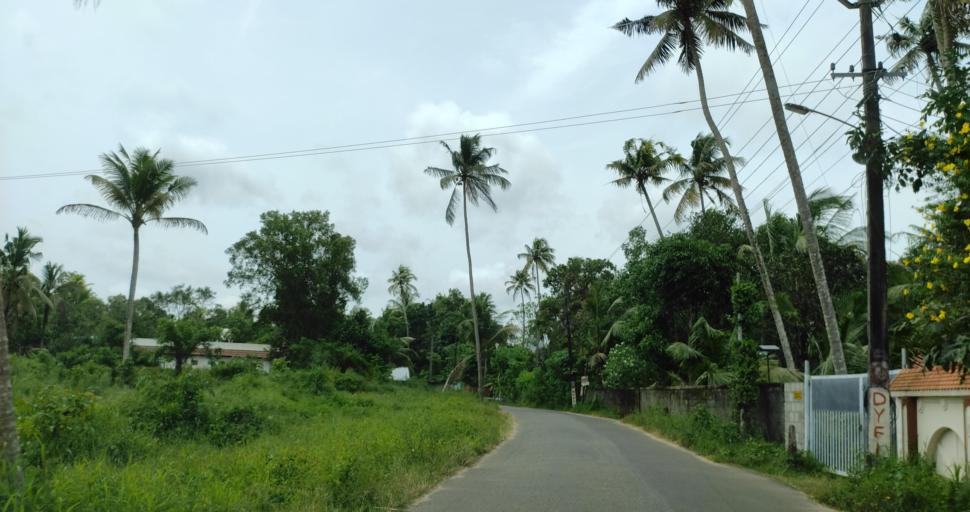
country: IN
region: Kerala
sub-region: Alappuzha
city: Shertallai
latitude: 9.6740
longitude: 76.3550
